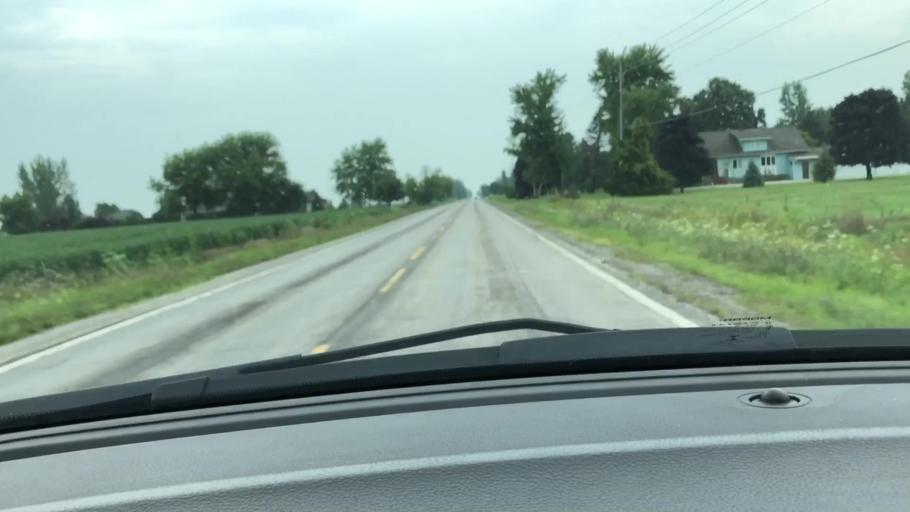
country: US
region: Michigan
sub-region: Saginaw County
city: Freeland
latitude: 43.5017
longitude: -84.0911
